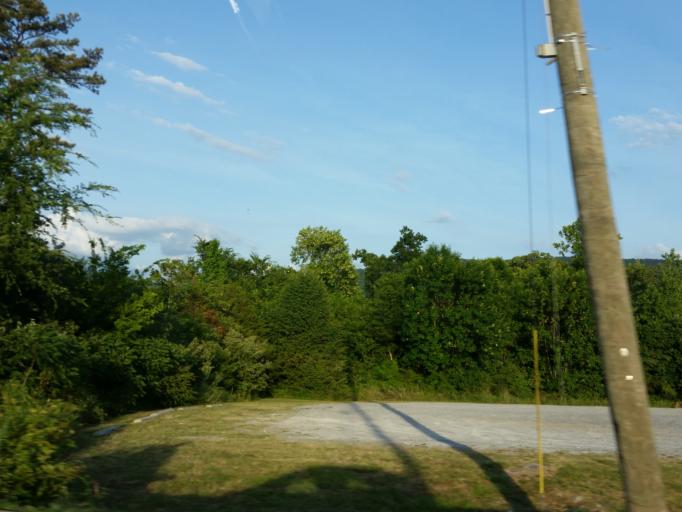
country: US
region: Georgia
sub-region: Dade County
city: Trenton
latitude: 34.8606
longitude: -85.5176
